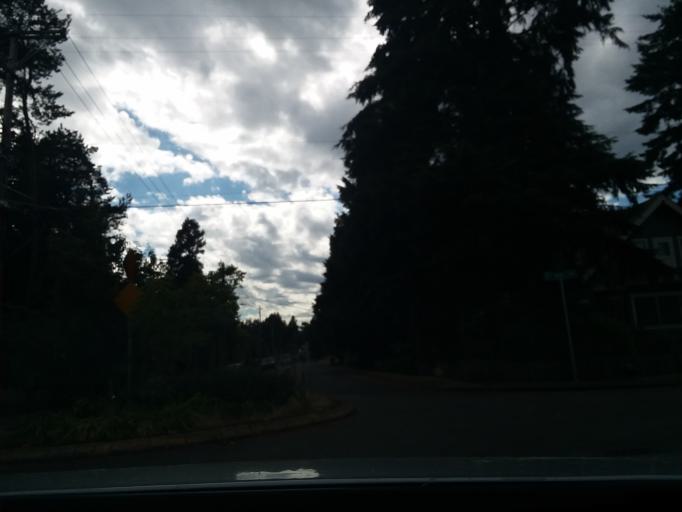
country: US
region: Washington
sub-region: King County
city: Shoreline
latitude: 47.6961
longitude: -122.3579
